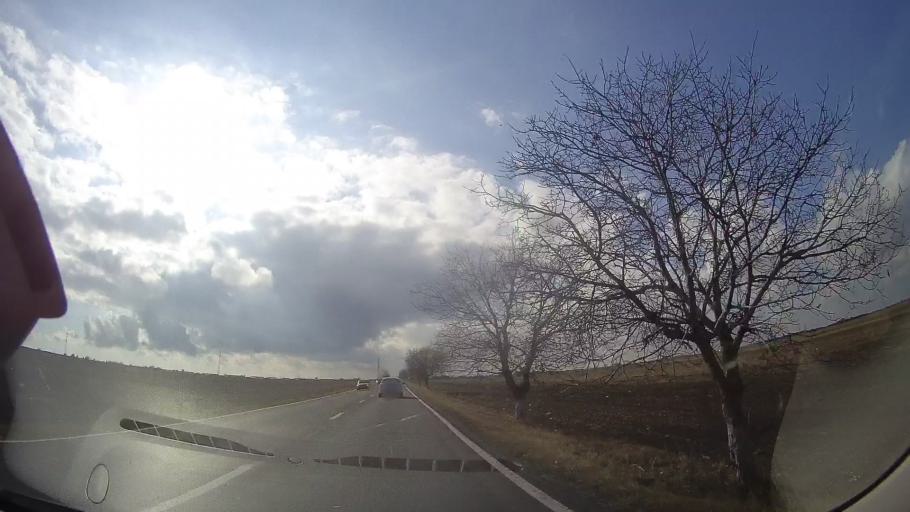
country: RO
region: Constanta
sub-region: Comuna Agigea
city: Agigea
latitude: 44.0775
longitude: 28.6013
